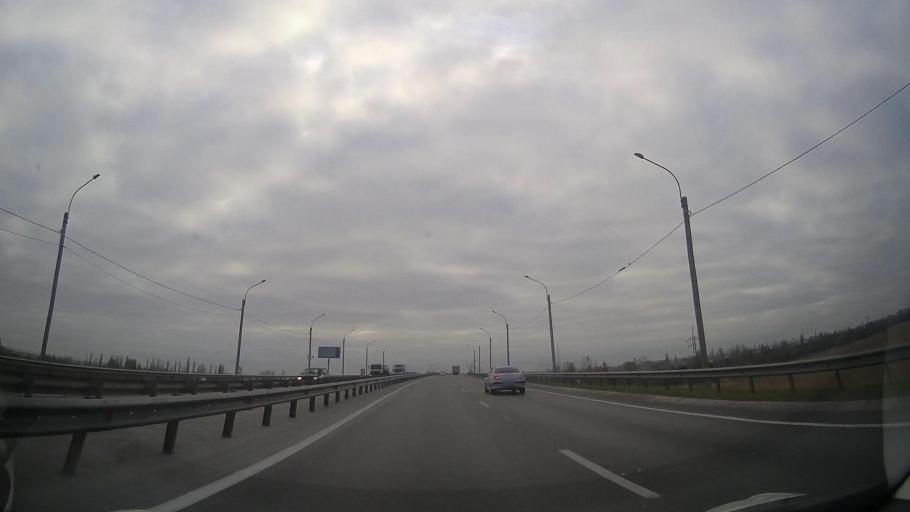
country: RU
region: Rostov
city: Bataysk
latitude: 47.1647
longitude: 39.7578
